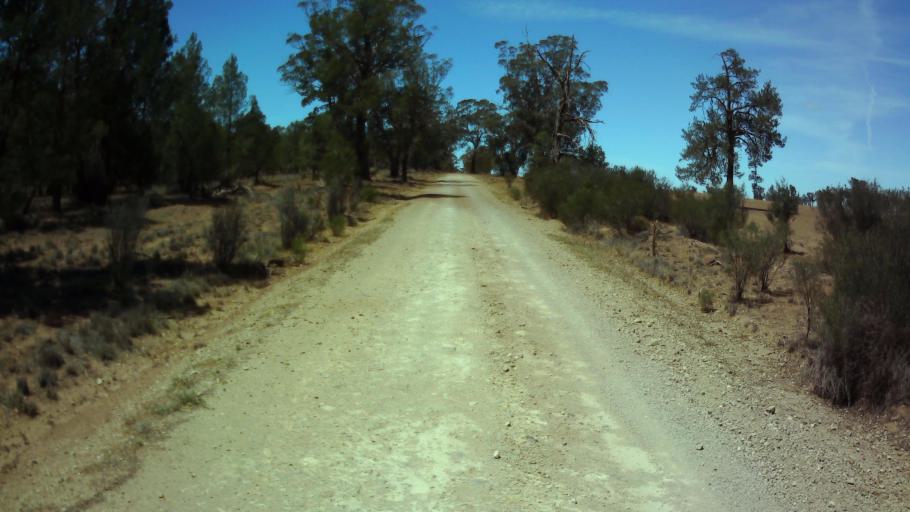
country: AU
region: New South Wales
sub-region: Forbes
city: Forbes
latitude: -33.7104
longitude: 147.7000
